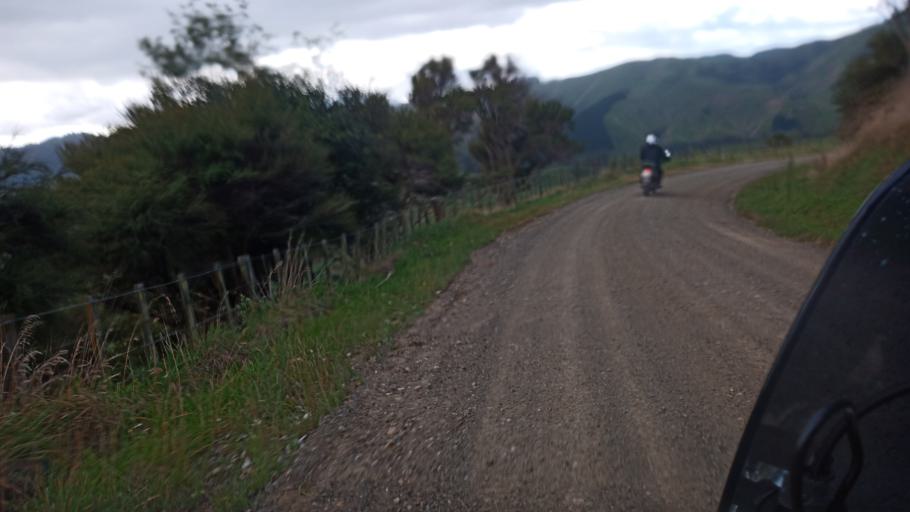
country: NZ
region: Gisborne
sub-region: Gisborne District
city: Gisborne
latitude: -38.4649
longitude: 177.6228
